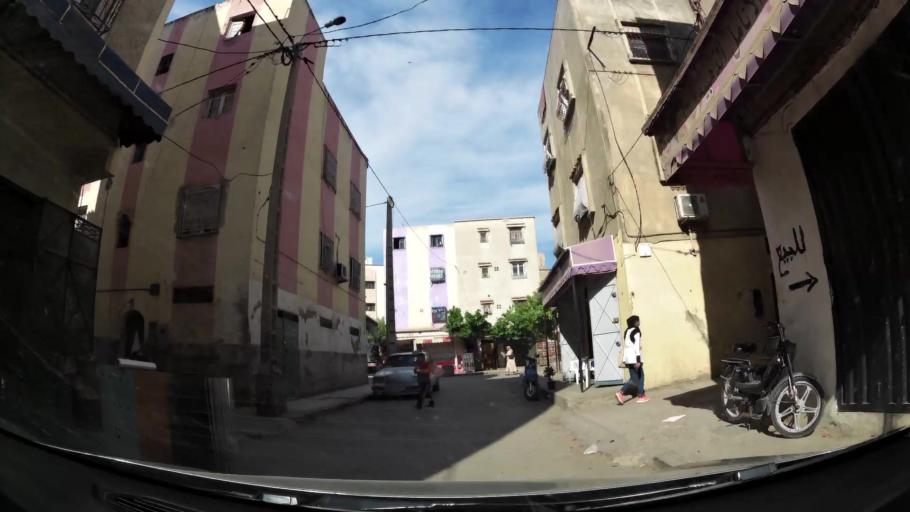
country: MA
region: Fes-Boulemane
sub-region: Fes
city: Fes
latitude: 34.0181
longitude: -5.0339
